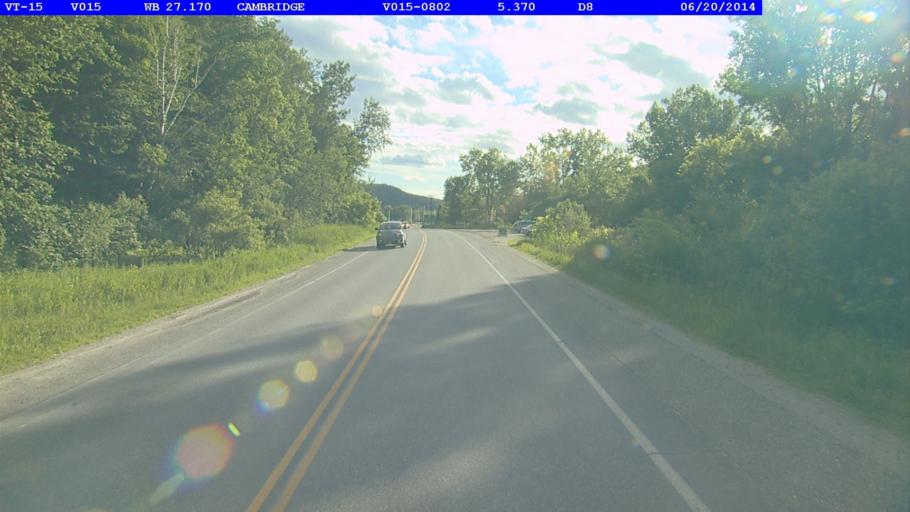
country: US
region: Vermont
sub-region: Lamoille County
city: Johnson
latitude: 44.6493
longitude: -72.8254
